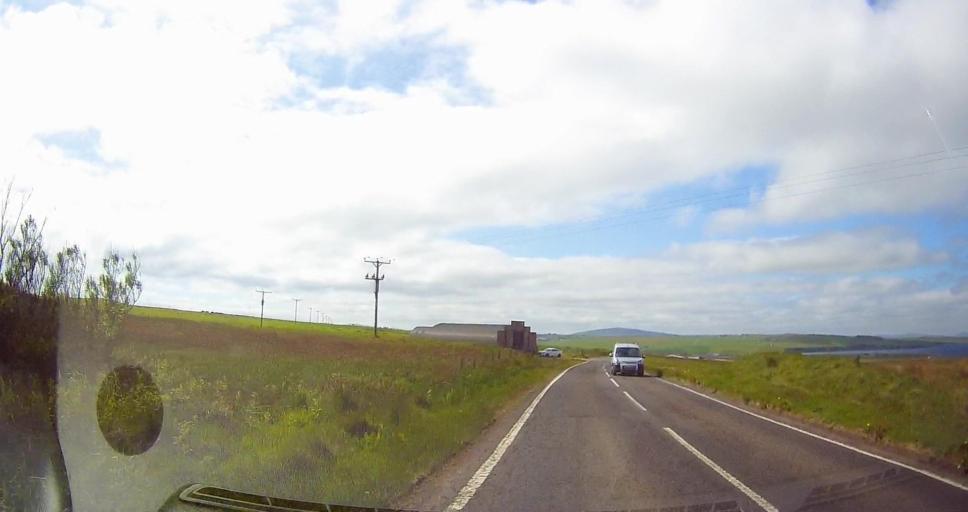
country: GB
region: Scotland
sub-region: Orkney Islands
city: Kirkwall
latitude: 58.9488
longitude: -2.8874
